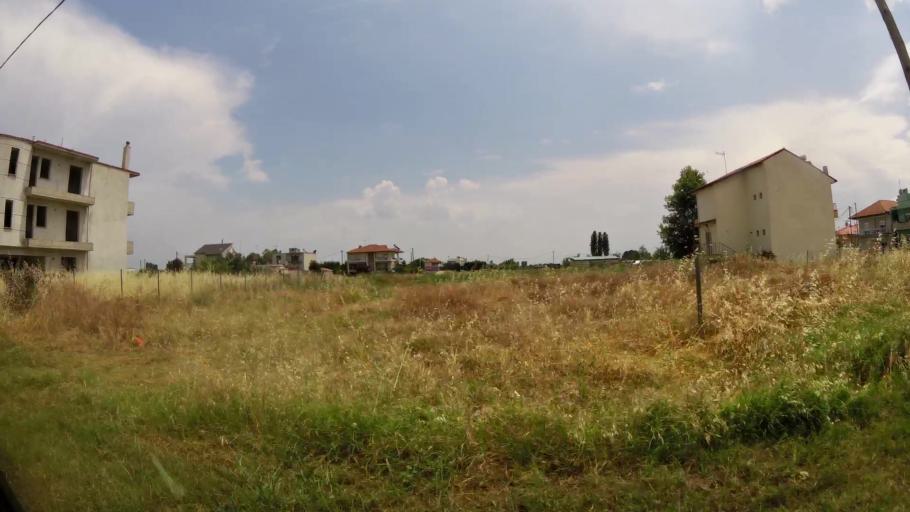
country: GR
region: Central Macedonia
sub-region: Nomos Pierias
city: Peristasi
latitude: 40.2721
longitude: 22.5455
